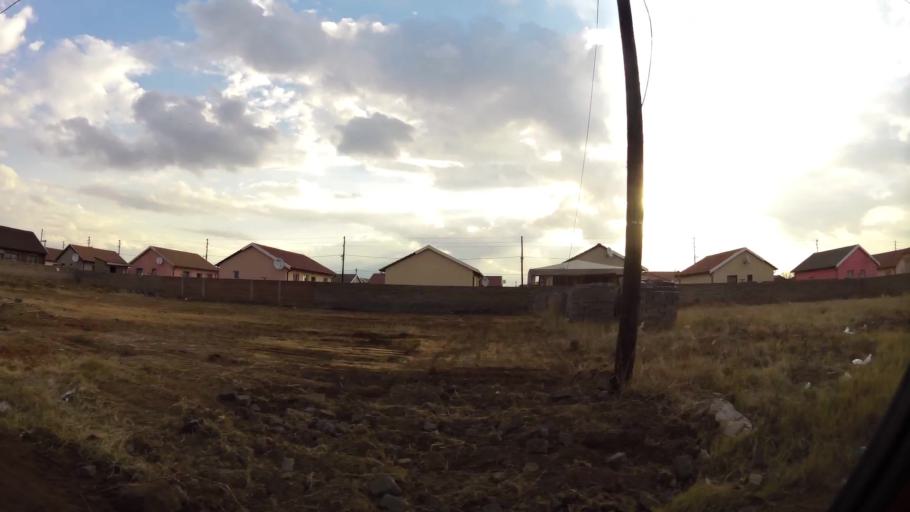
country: ZA
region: Gauteng
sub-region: Sedibeng District Municipality
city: Vanderbijlpark
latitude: -26.6116
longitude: 27.8137
